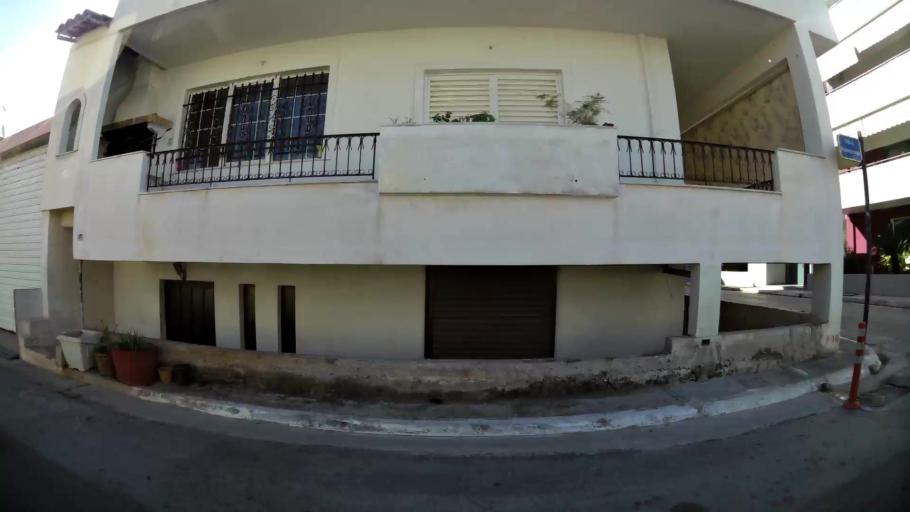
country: GR
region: Attica
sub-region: Nomarchia Anatolikis Attikis
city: Koropi
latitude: 37.9102
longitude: 23.8702
